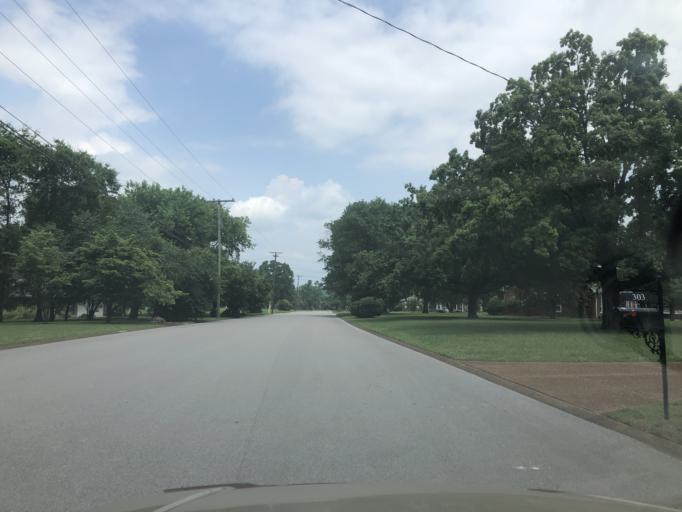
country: US
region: Tennessee
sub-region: Davidson County
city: Lakewood
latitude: 36.2372
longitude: -86.6220
